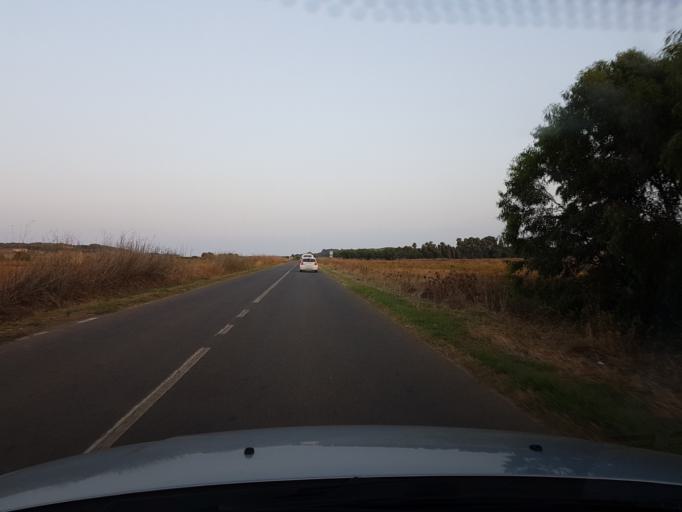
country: IT
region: Sardinia
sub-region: Provincia di Oristano
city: Cabras
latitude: 39.9451
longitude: 8.4342
